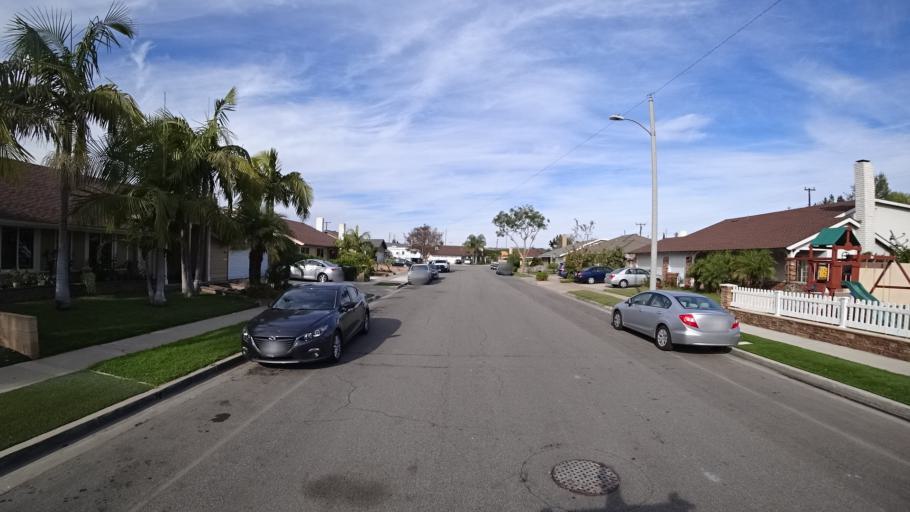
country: US
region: California
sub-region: Orange County
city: Garden Grove
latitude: 33.7722
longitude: -117.9056
